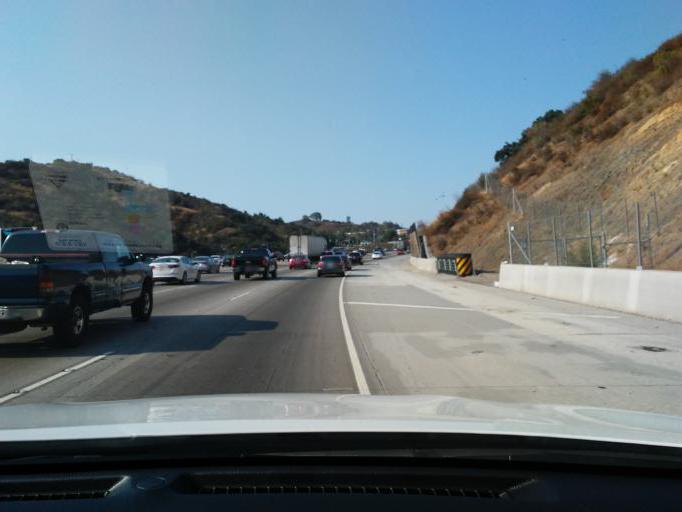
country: US
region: California
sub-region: Los Angeles County
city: Sherman Oaks
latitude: 34.1184
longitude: -118.4813
